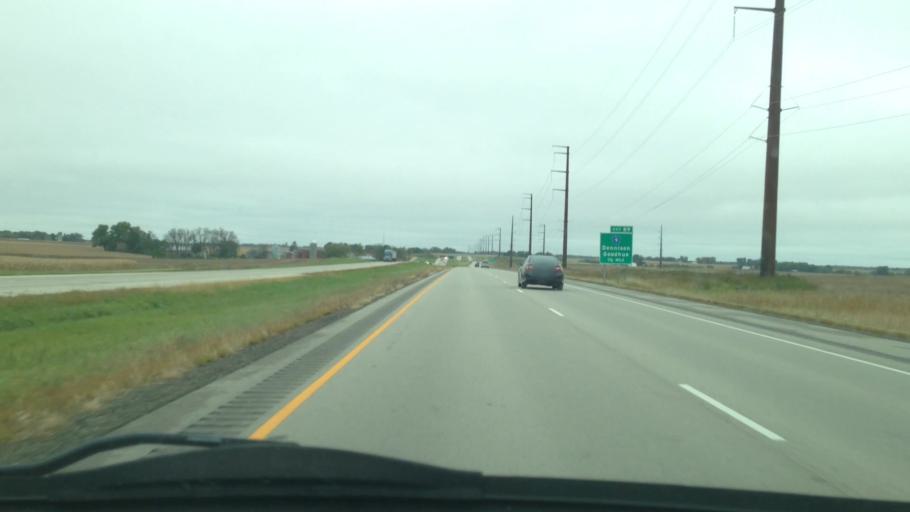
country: US
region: Minnesota
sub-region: Goodhue County
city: Wanamingo
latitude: 44.3908
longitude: -92.8319
